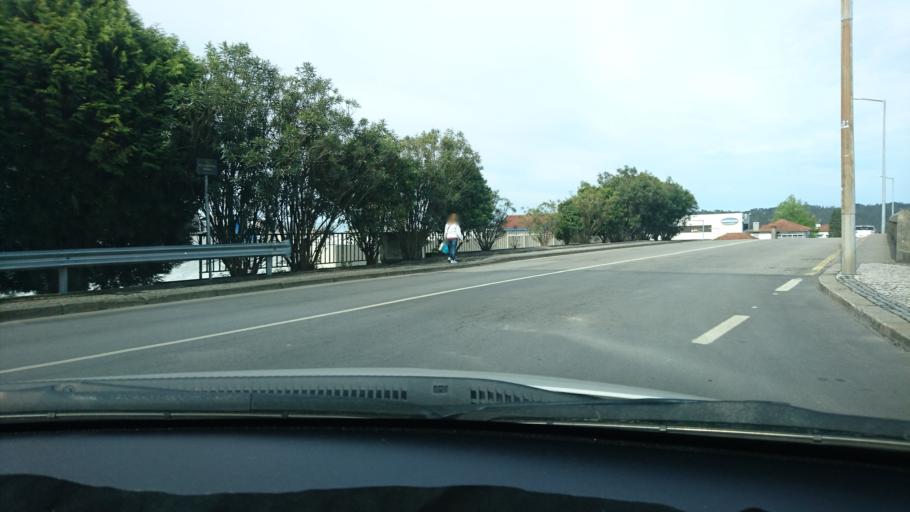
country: PT
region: Aveiro
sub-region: Oliveira de Azemeis
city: Oliveira de Azemeis
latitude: 40.8393
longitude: -8.4814
